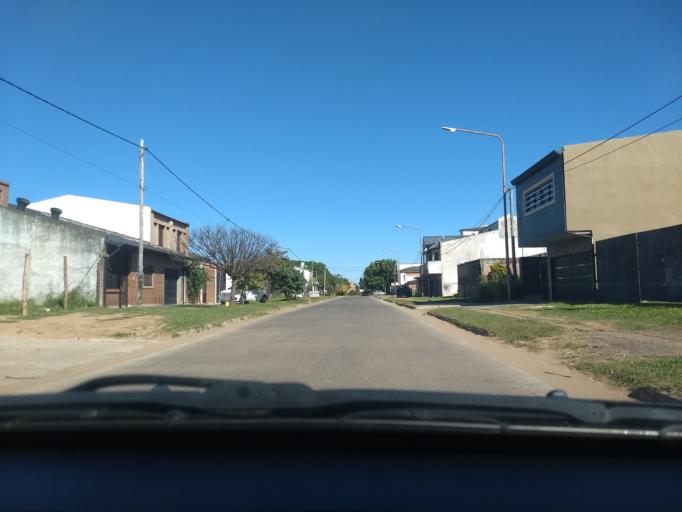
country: AR
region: Corrientes
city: Corrientes
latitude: -27.4798
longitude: -58.7891
